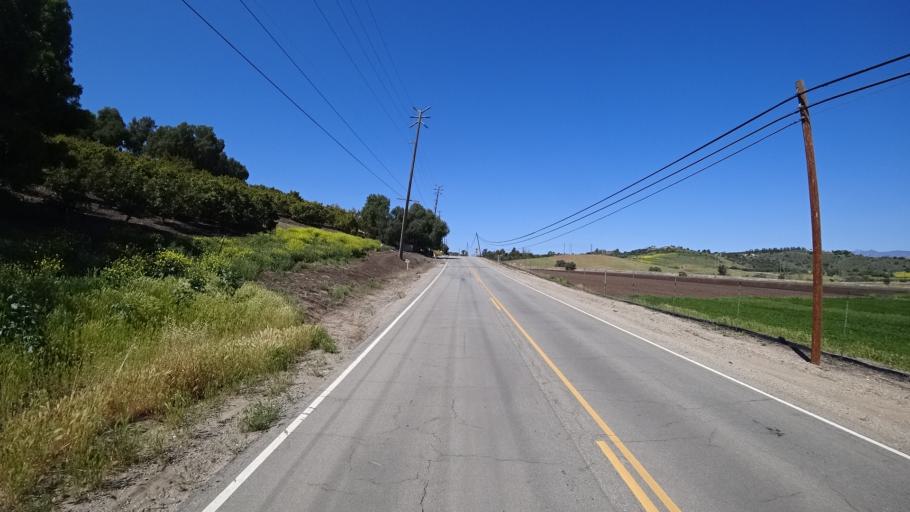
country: US
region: California
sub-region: Ventura County
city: Moorpark
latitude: 34.2500
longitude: -118.8611
